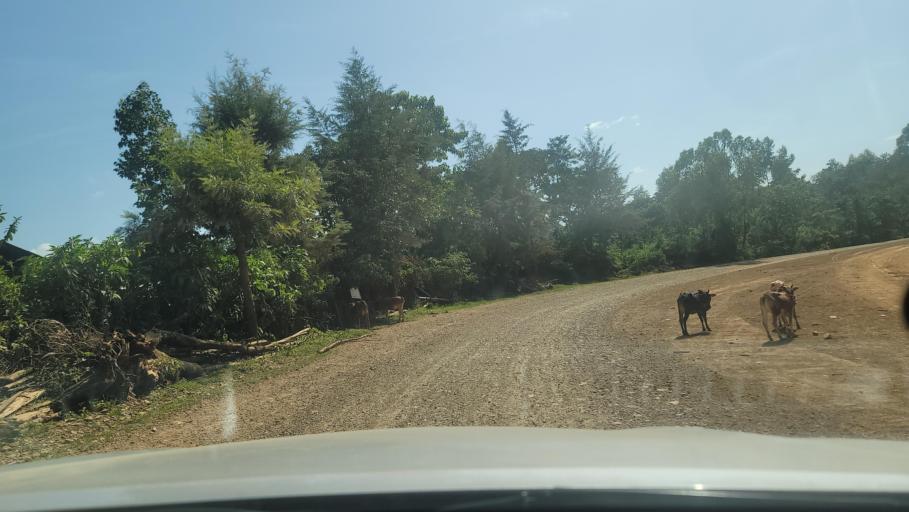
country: ET
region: Oromiya
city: Agaro
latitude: 7.7850
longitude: 36.4077
